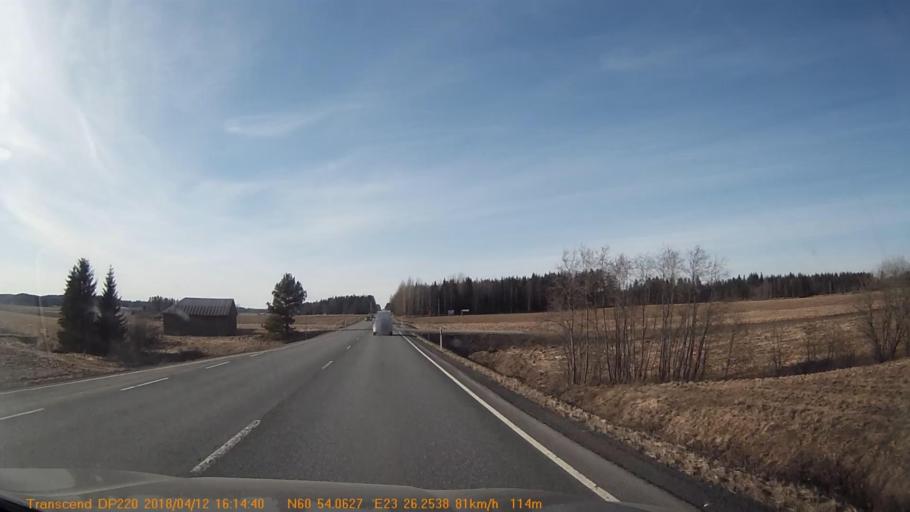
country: FI
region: Haeme
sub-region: Forssa
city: Humppila
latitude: 60.9012
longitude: 23.4373
